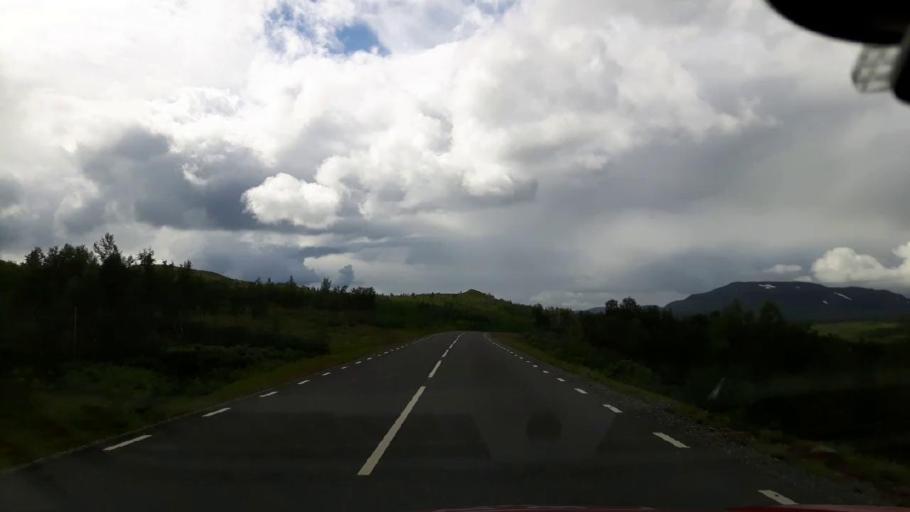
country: NO
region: Nordland
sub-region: Hattfjelldal
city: Hattfjelldal
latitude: 65.0089
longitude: 14.2700
